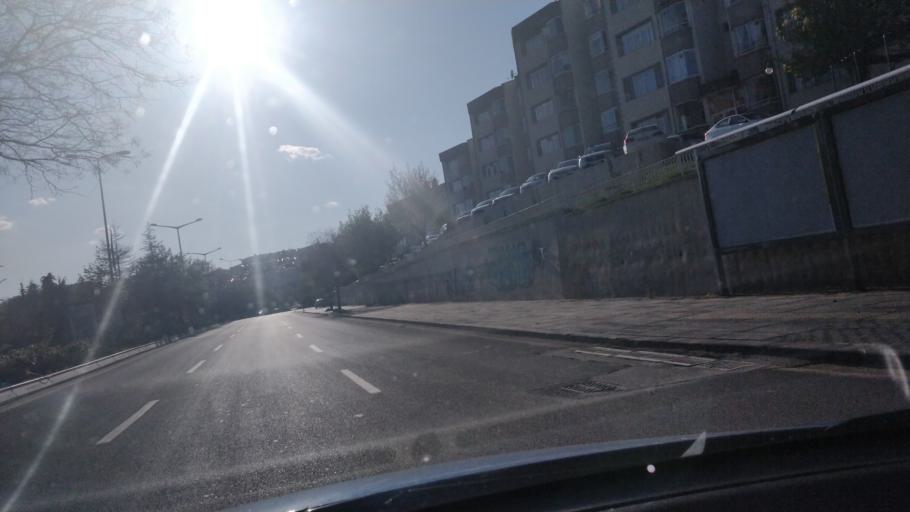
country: TR
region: Ankara
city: Batikent
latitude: 39.9580
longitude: 32.7233
